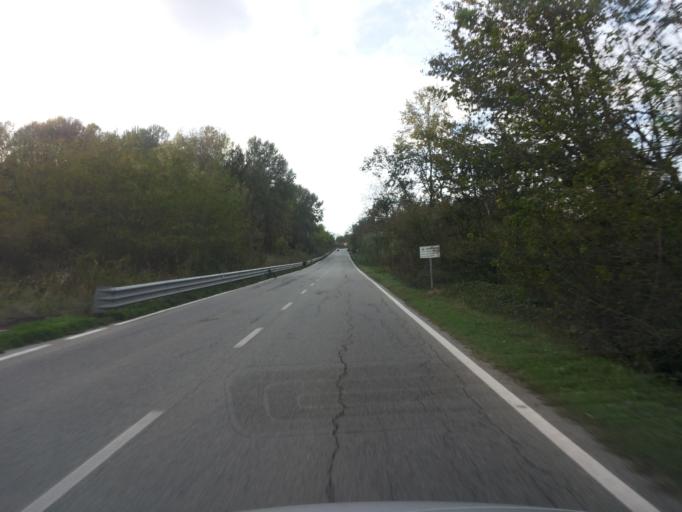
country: IT
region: Piedmont
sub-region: Provincia di Alessandria
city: Ozzano Monferrato
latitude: 45.1056
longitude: 8.3930
